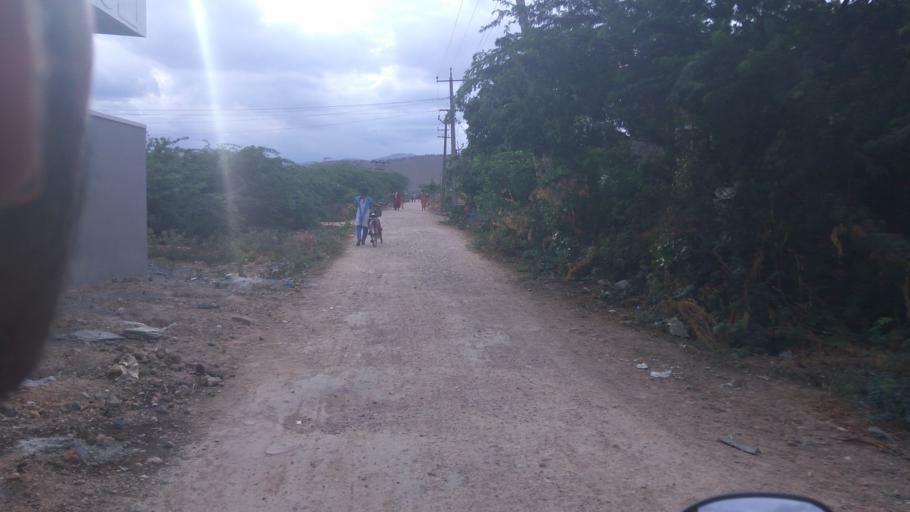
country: IN
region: Andhra Pradesh
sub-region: Prakasam
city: Cumbum
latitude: 15.5886
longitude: 79.1107
